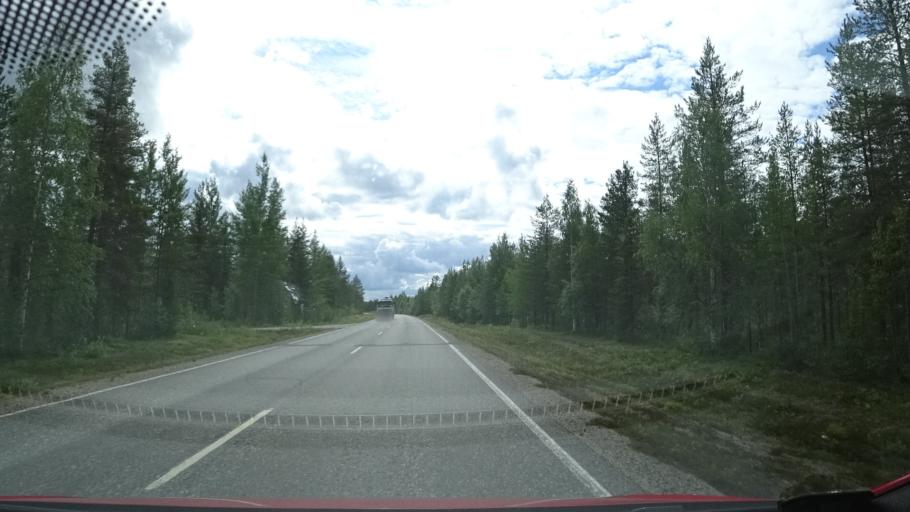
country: FI
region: Lapland
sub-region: Tunturi-Lappi
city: Kittilae
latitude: 67.5117
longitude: 24.8999
